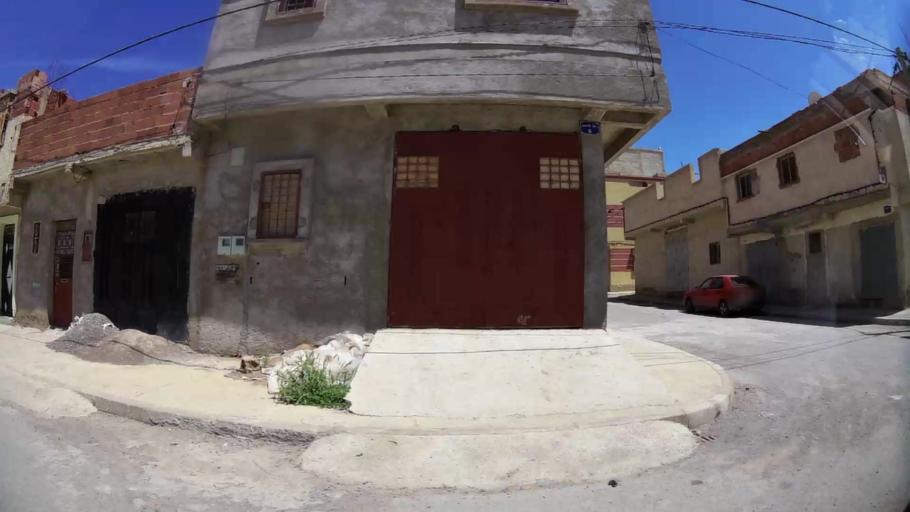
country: MA
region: Oriental
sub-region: Oujda-Angad
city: Oujda
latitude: 34.6898
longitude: -1.9538
